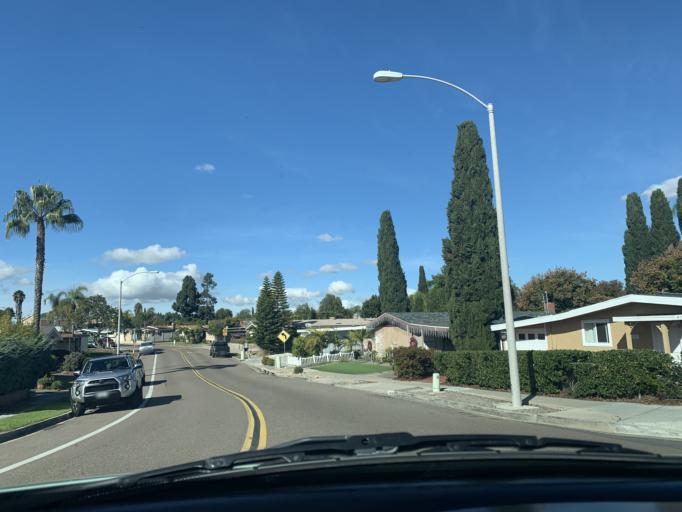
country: US
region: California
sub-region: San Diego County
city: San Diego
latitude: 32.8037
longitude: -117.1351
